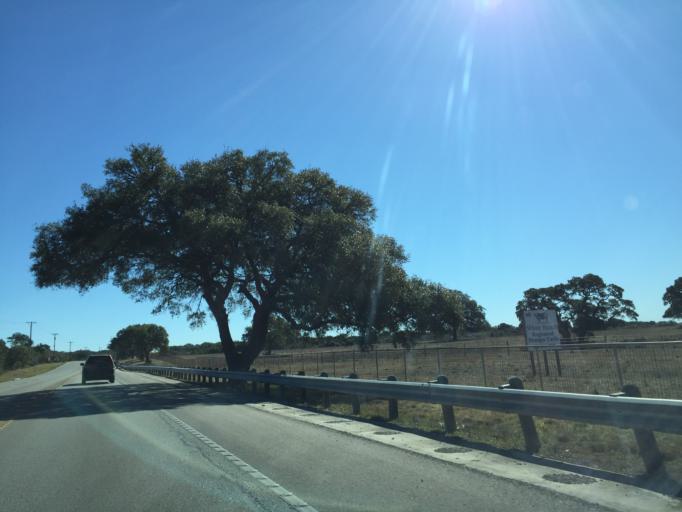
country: US
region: Texas
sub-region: Comal County
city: Canyon Lake
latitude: 29.7784
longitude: -98.3140
